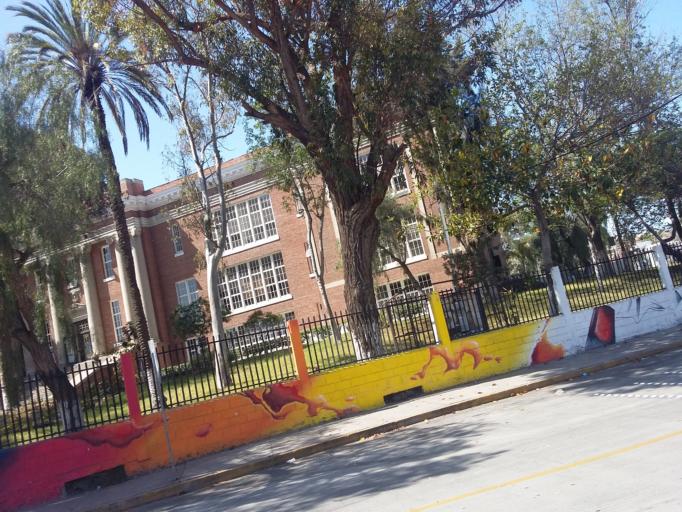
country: MX
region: Baja California
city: Tijuana
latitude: 32.5324
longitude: -117.0519
